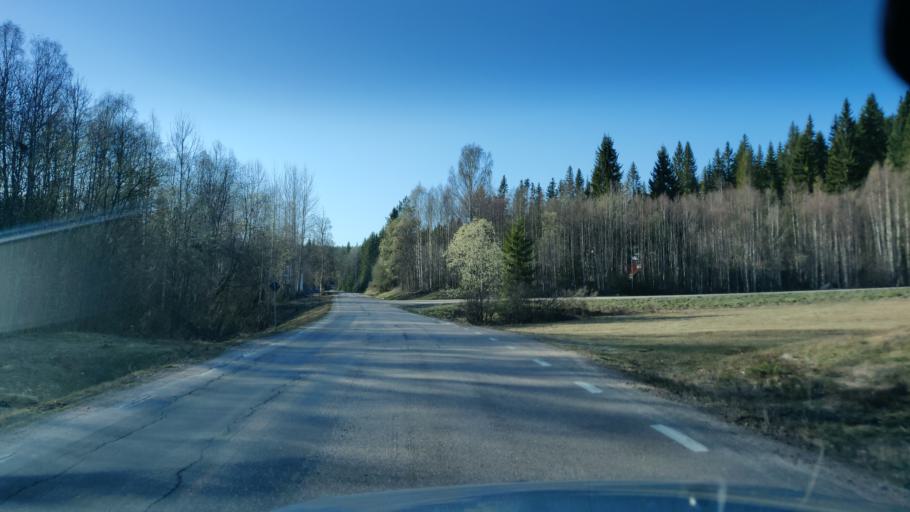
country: SE
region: Vaermland
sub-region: Munkfors Kommun
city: Munkfors
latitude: 59.9834
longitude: 13.4024
